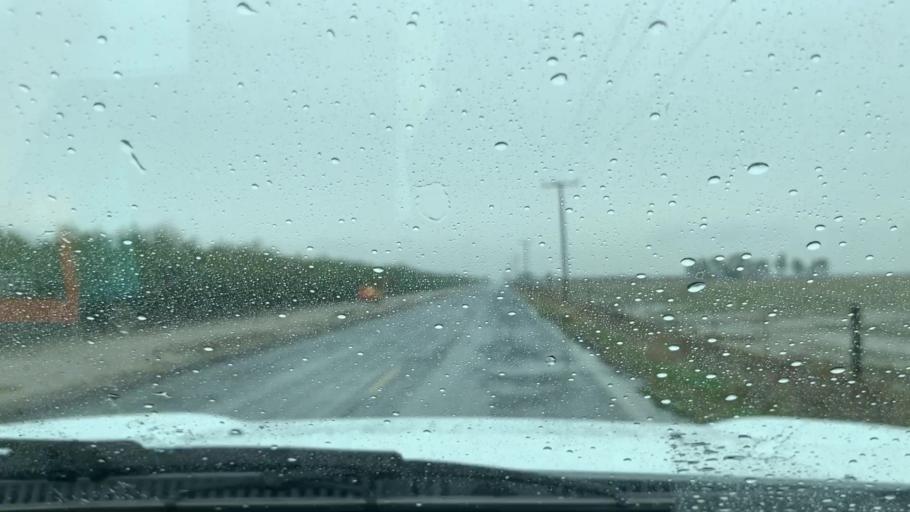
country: US
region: California
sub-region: Tulare County
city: Earlimart
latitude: 35.8919
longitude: -119.3326
